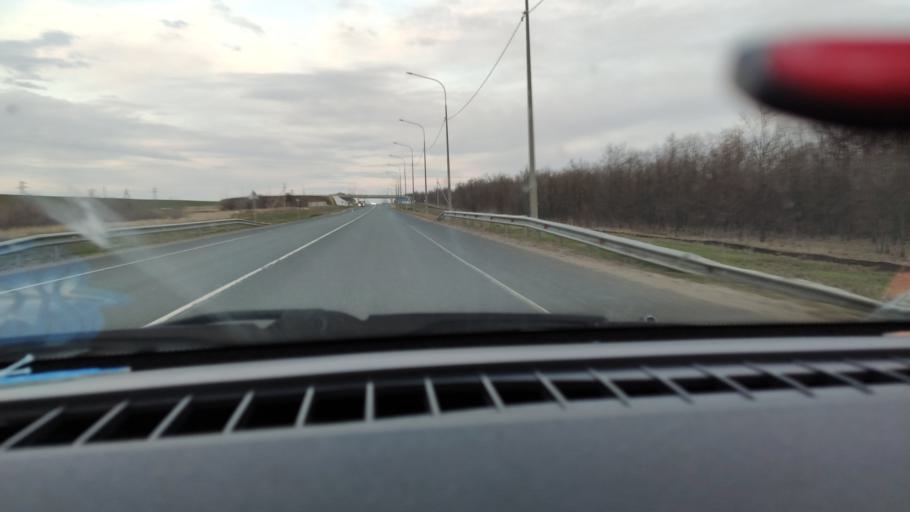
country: RU
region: Saratov
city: Yelshanka
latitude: 51.8251
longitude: 46.2950
